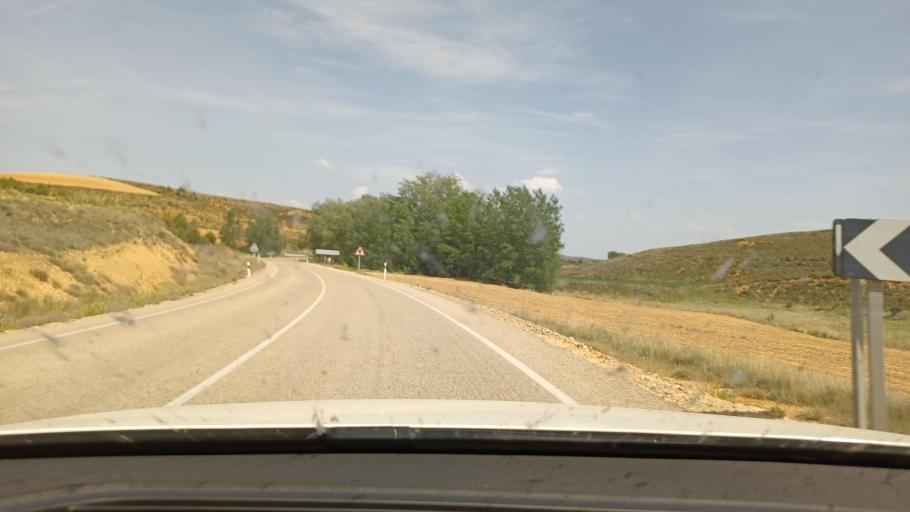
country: ES
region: Castille and Leon
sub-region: Provincia de Soria
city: Canamaque
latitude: 41.3998
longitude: -2.2097
